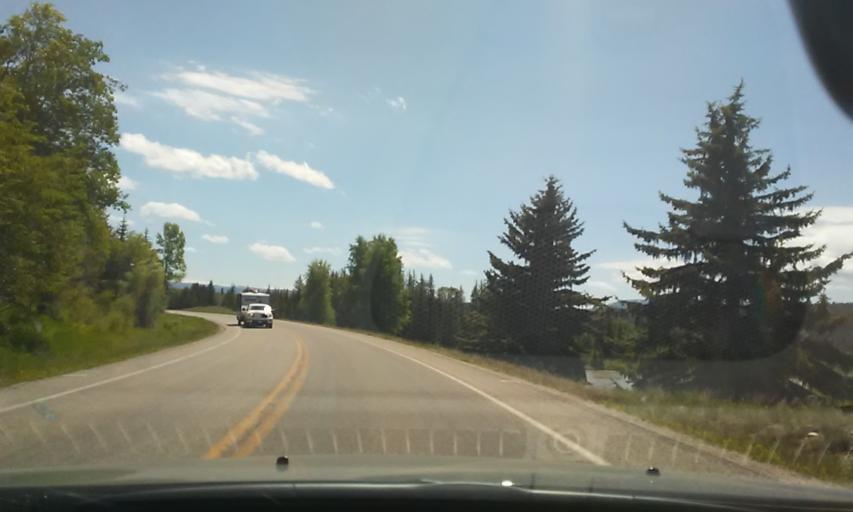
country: US
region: Wyoming
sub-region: Teton County
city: Jackson
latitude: 43.8376
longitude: -110.5017
